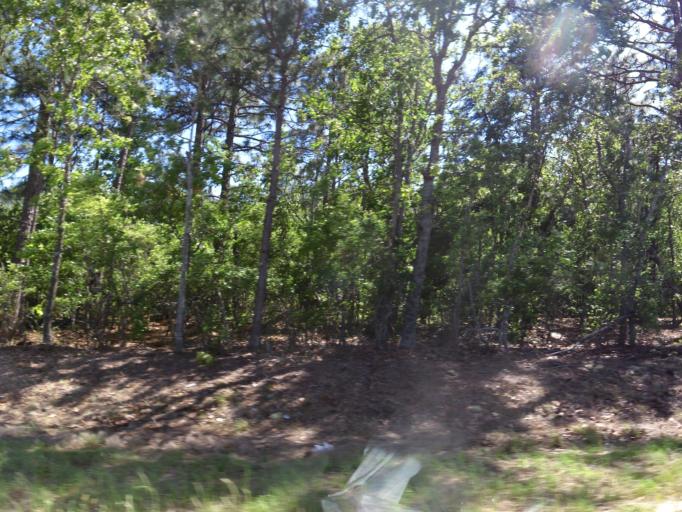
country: US
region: South Carolina
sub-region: Aiken County
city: New Ellenton
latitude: 33.5134
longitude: -81.5719
